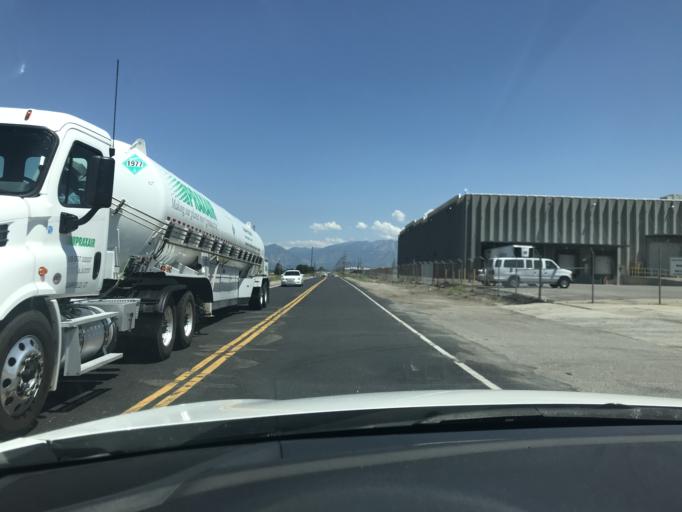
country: US
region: Utah
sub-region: Salt Lake County
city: Magna
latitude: 40.6820
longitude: -112.0820
